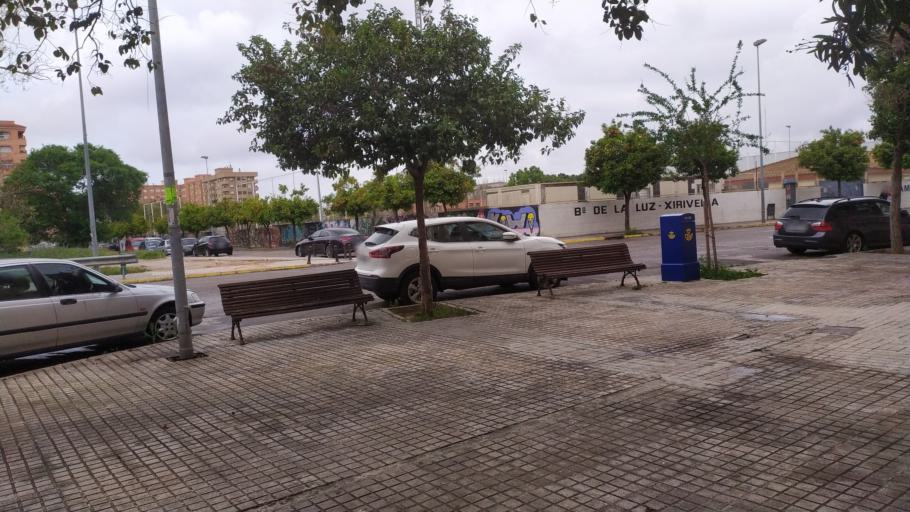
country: ES
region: Valencia
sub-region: Provincia de Valencia
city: Mislata
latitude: 39.4669
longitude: -0.4144
